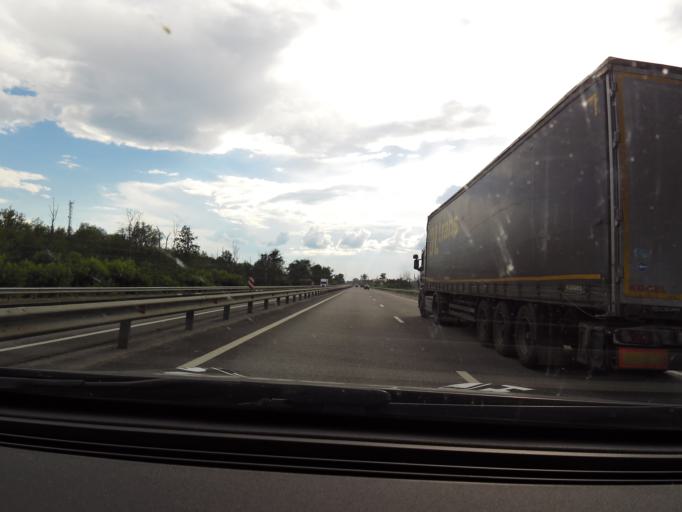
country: RU
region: Vladimir
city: Galitsy
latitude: 56.2320
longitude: 42.8092
